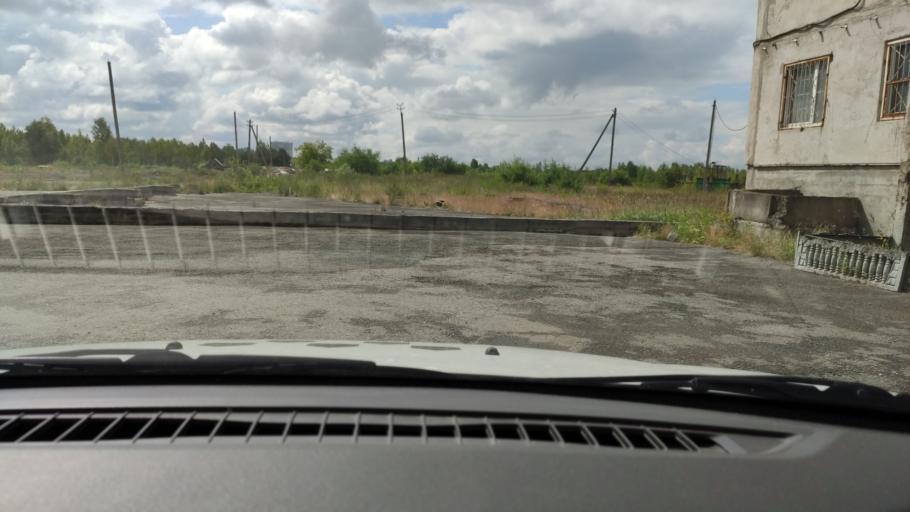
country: RU
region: Perm
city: Perm
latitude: 58.0332
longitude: 56.1884
